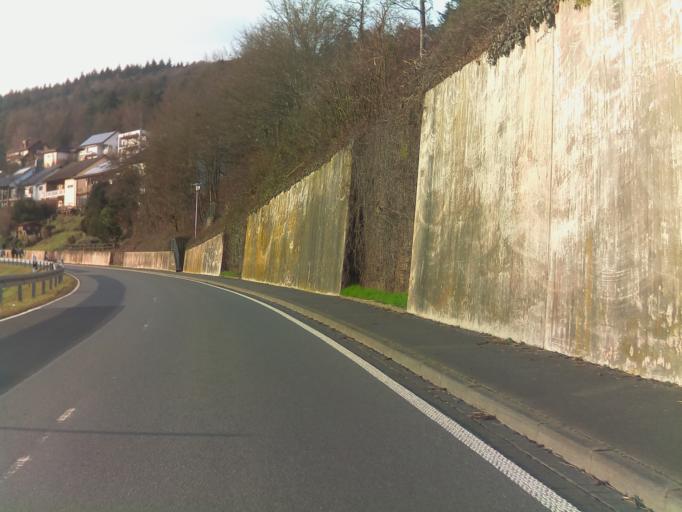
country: DE
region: Bavaria
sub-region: Regierungsbezirk Unterfranken
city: Laudenbach
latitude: 49.7449
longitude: 9.1706
